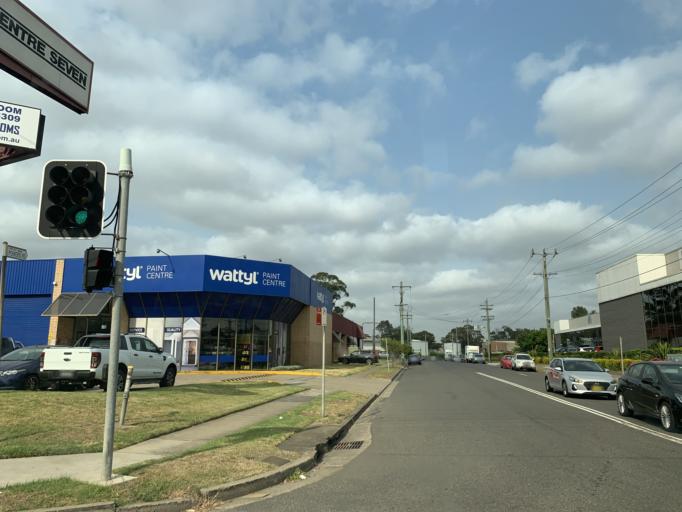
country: AU
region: New South Wales
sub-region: Holroyd
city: Girraween
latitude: -33.7739
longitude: 150.9443
